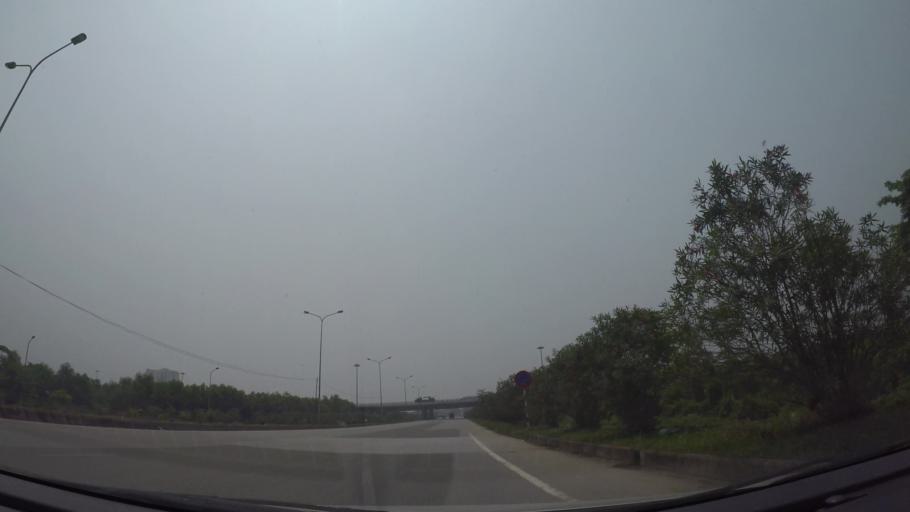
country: VN
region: Ha Noi
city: Lien Quan
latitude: 20.9918
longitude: 105.5243
